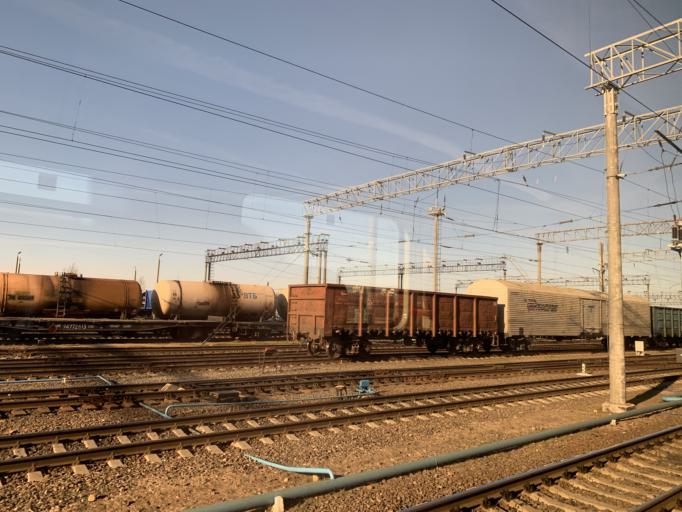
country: BY
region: Minsk
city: Maladzyechna
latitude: 54.3168
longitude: 26.8234
